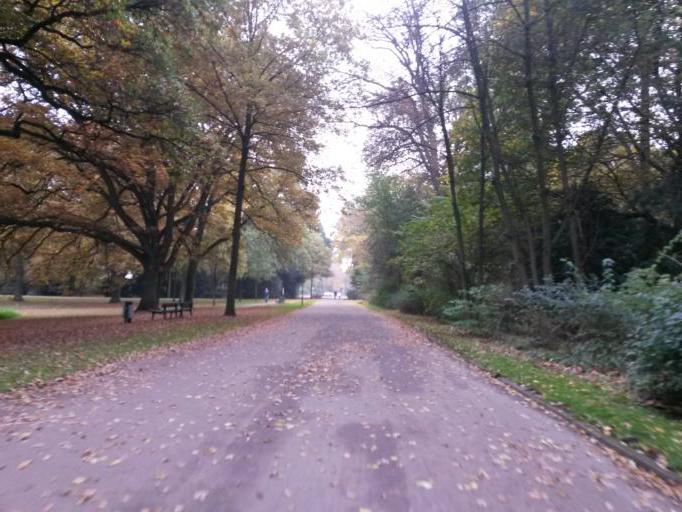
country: DE
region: Bremen
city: Bremen
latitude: 53.0932
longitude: 8.8295
